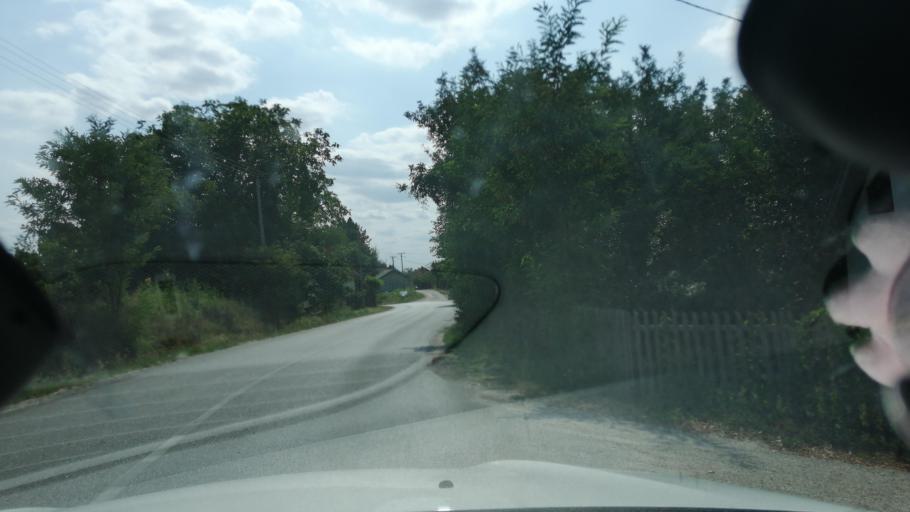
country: RS
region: Central Serbia
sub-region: Moravicki Okrug
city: Cacak
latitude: 43.8233
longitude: 20.2807
